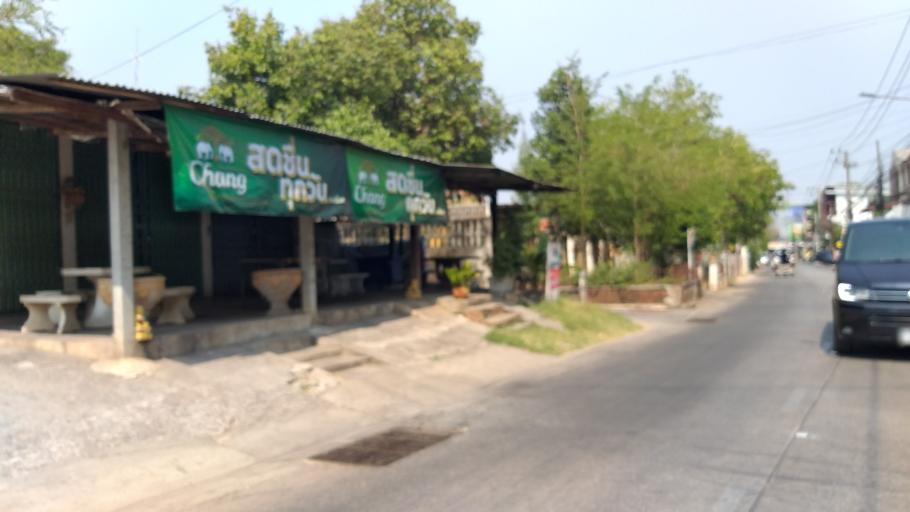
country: TH
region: Changwat Udon Thani
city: Udon Thani
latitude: 17.4059
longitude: 102.7757
